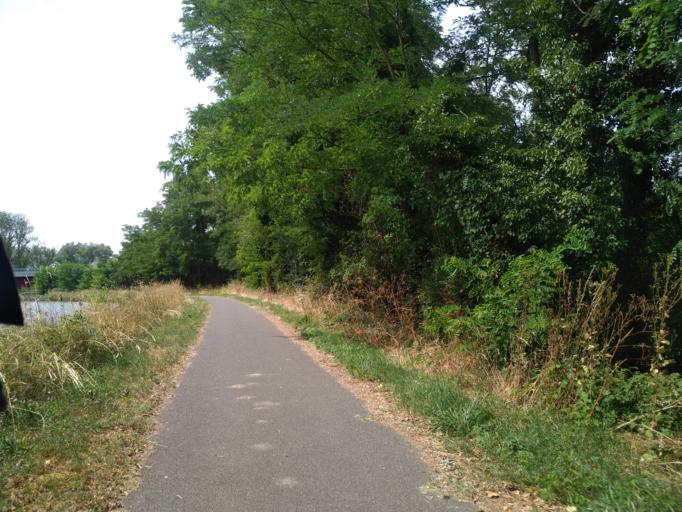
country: FR
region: Auvergne
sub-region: Departement de l'Allier
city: Diou
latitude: 46.5360
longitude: 3.7647
